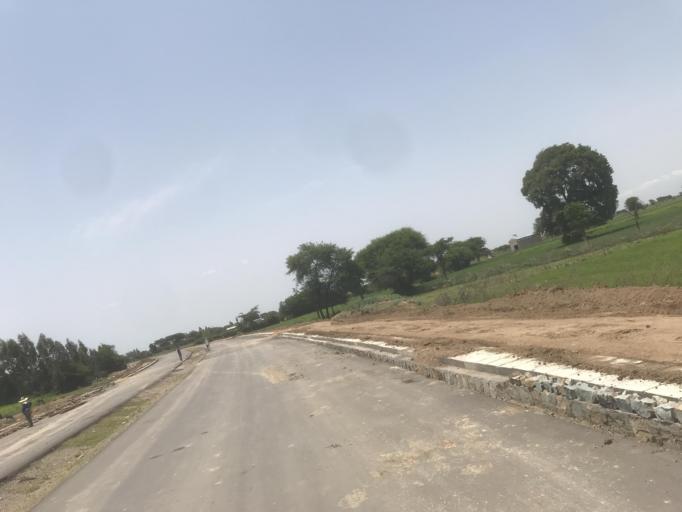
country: ET
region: Oromiya
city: Mojo
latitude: 8.2974
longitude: 38.9398
